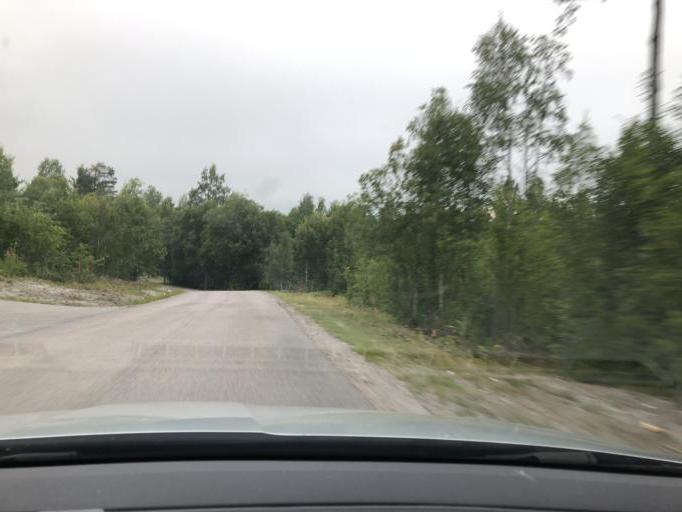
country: SE
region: Vaesternorrland
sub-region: Sundsvalls Kommun
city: Sundsvall
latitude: 62.4049
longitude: 17.3050
